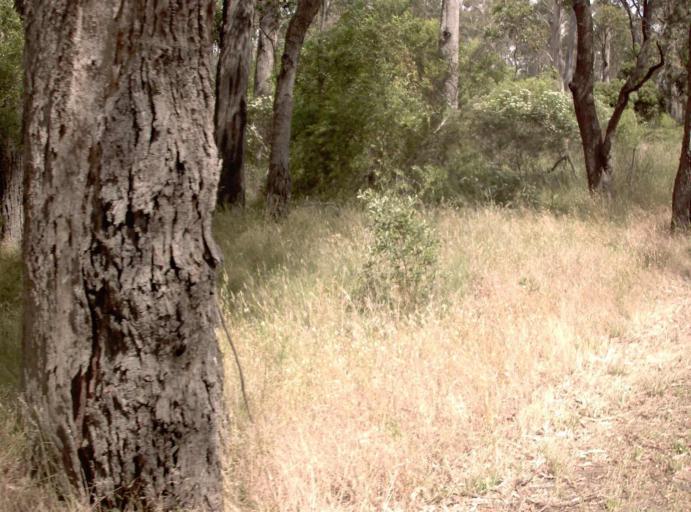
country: AU
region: Victoria
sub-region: Latrobe
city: Traralgon
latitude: -38.2904
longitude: 146.5397
